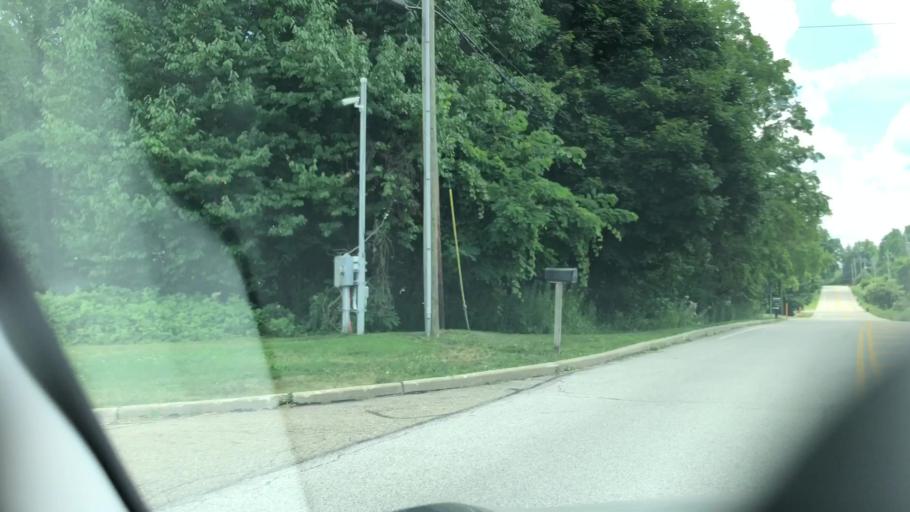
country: US
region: Ohio
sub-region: Summit County
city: Montrose-Ghent
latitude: 41.1256
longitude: -81.6485
